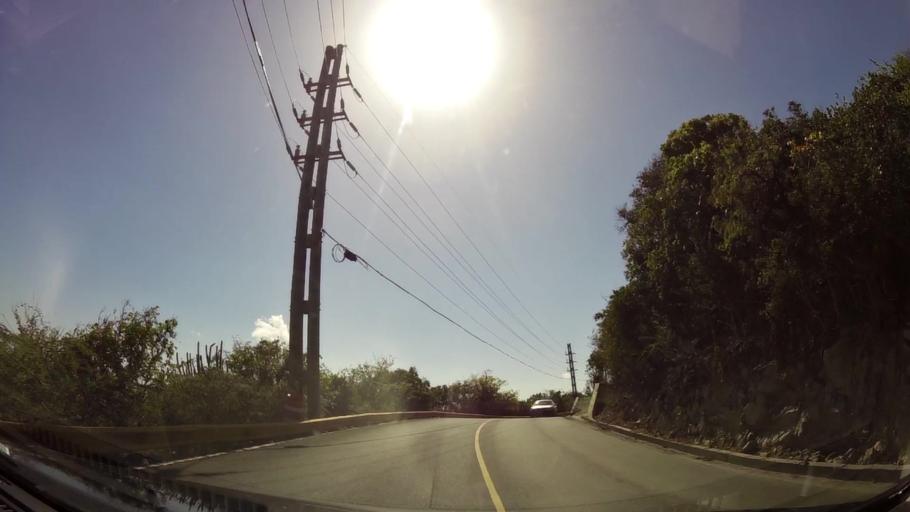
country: VG
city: Tortola
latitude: 18.4131
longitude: -64.5884
